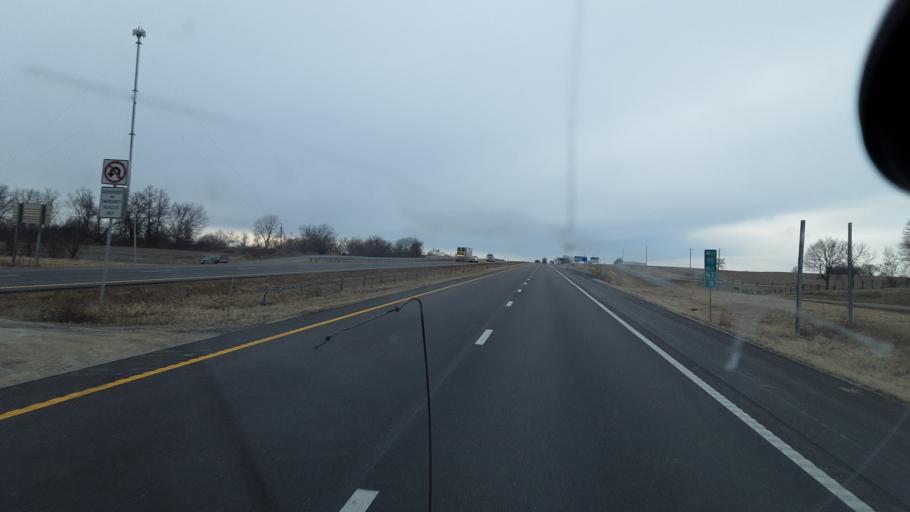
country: US
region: Missouri
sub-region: Saline County
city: Sweet Springs
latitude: 38.9762
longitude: -93.3987
